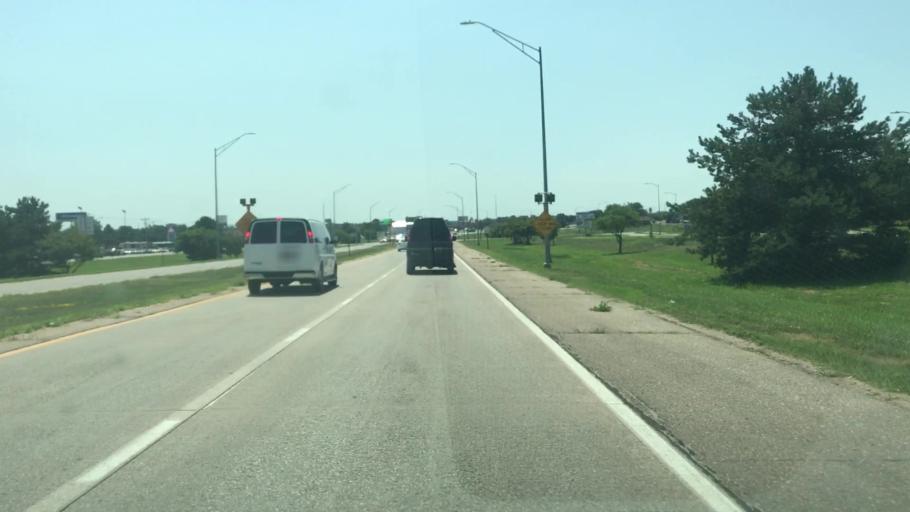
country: US
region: Nebraska
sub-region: Adams County
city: Hastings
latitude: 40.6159
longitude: -98.3832
